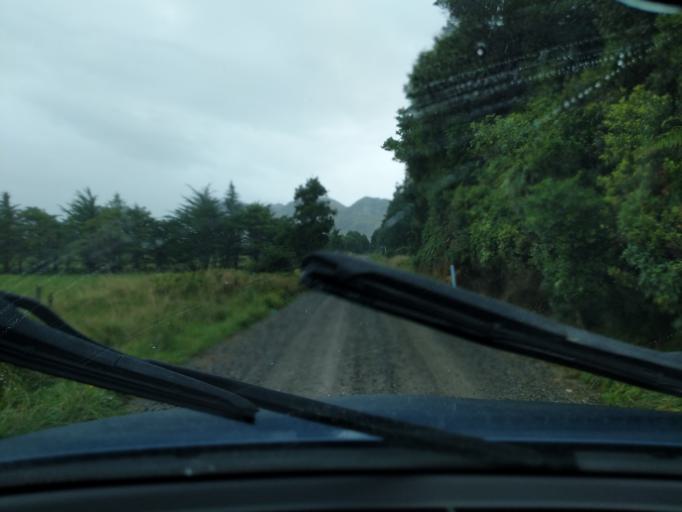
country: NZ
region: Tasman
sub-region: Tasman District
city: Takaka
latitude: -40.6512
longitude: 172.4656
